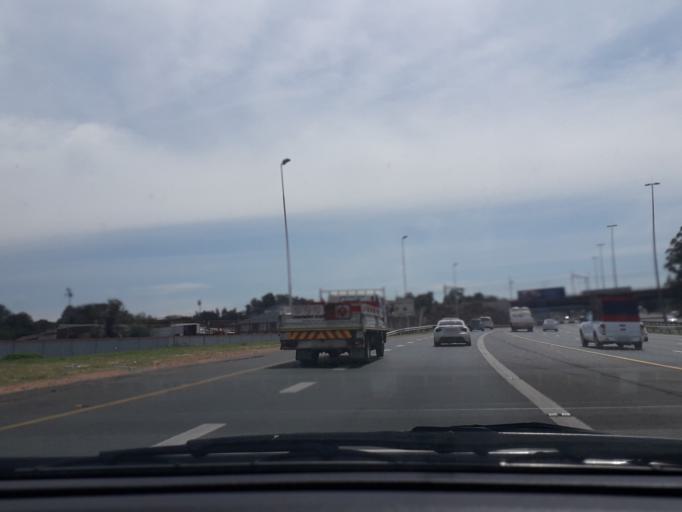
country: ZA
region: Gauteng
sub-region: City of Johannesburg Metropolitan Municipality
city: Roodepoort
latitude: -26.1835
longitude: 27.9451
